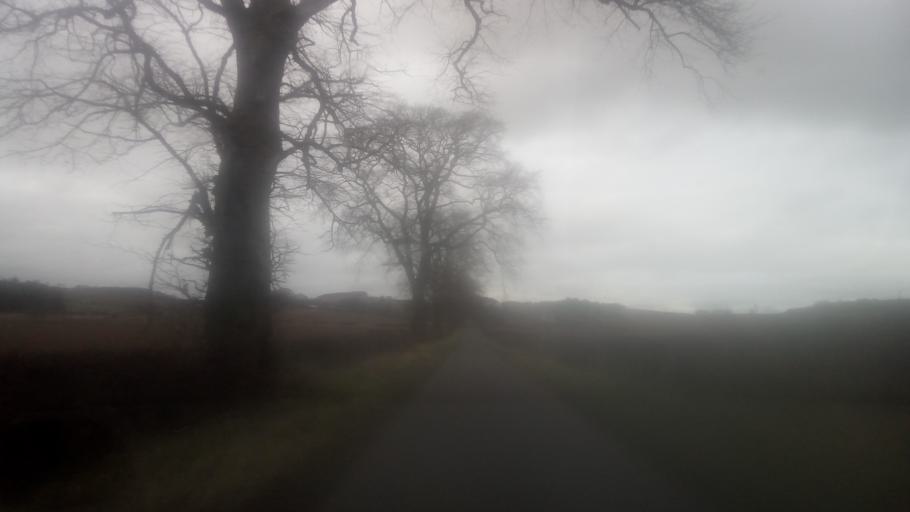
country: GB
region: Scotland
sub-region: The Scottish Borders
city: Jedburgh
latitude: 55.4745
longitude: -2.4849
